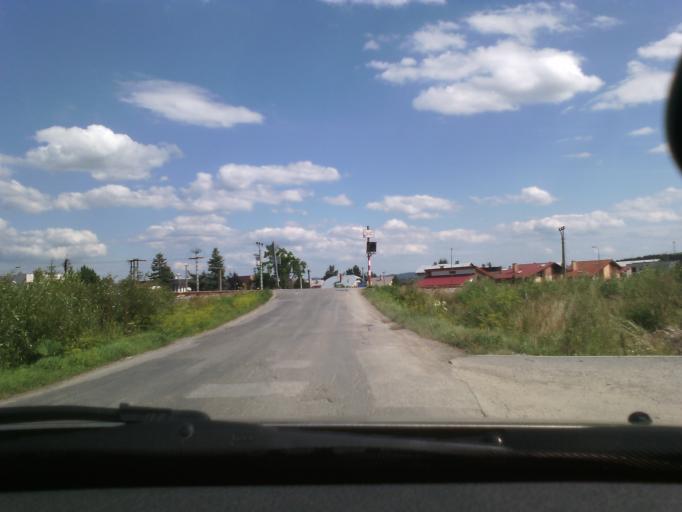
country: SK
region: Presovsky
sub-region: Okres Poprad
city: Poprad
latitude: 49.1200
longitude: 20.3506
